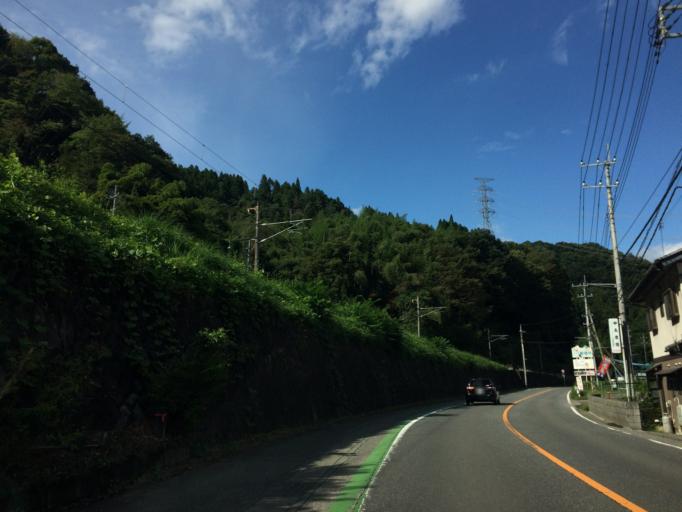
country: JP
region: Gunma
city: Nakanojomachi
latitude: 36.5585
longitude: 138.8102
